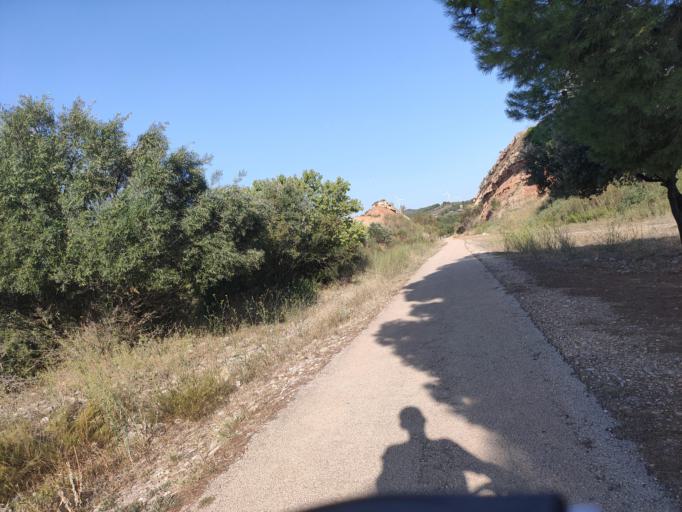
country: ES
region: Catalonia
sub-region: Provincia de Tarragona
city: Bot
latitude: 41.0075
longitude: 0.3826
